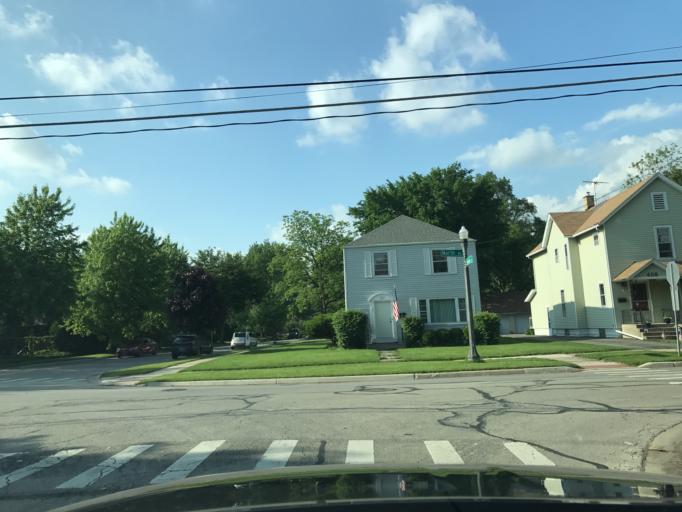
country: US
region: Illinois
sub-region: DuPage County
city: Naperville
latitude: 41.7781
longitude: -88.1421
